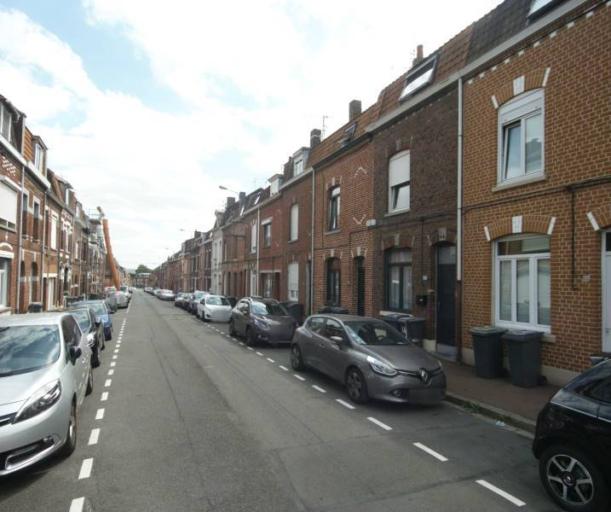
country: FR
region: Nord-Pas-de-Calais
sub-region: Departement du Nord
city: Mouvaux
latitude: 50.7031
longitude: 3.1503
